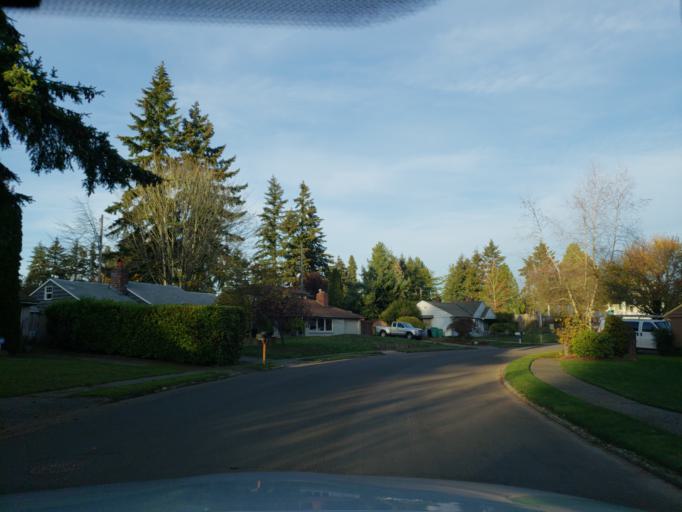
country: US
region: Washington
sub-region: King County
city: Shoreline
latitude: 47.7405
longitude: -122.3407
